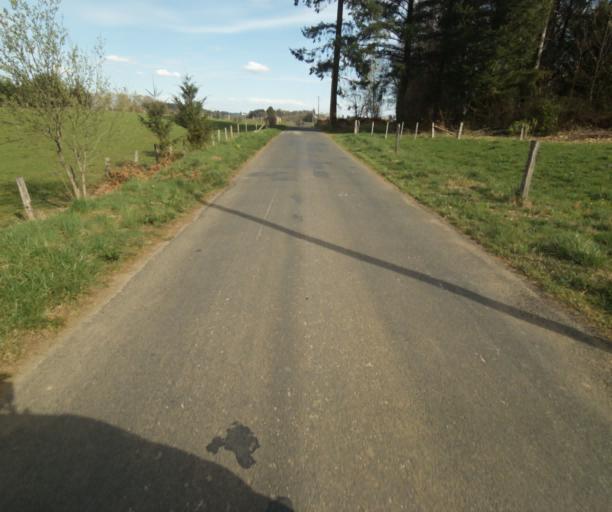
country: FR
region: Limousin
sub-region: Departement de la Correze
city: Seilhac
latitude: 45.3312
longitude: 1.7276
